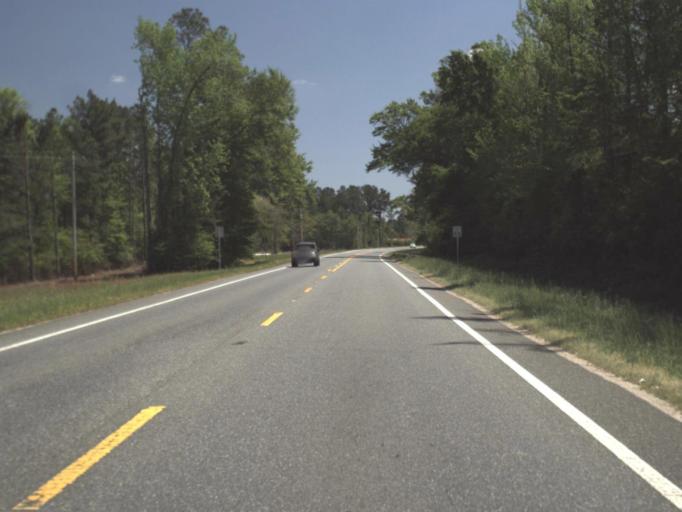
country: US
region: Florida
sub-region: Escambia County
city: Century
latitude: 30.9769
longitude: -87.2479
